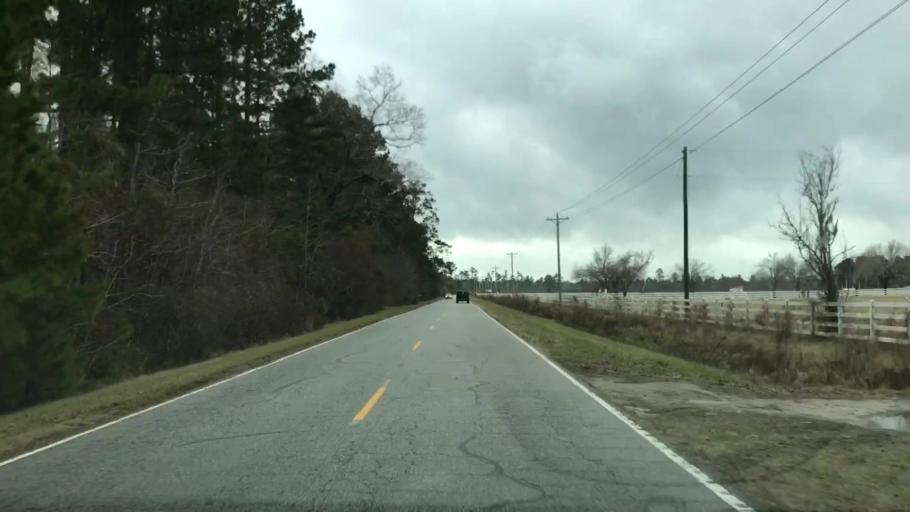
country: US
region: South Carolina
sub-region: Florence County
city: Johnsonville
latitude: 33.6558
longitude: -79.4192
